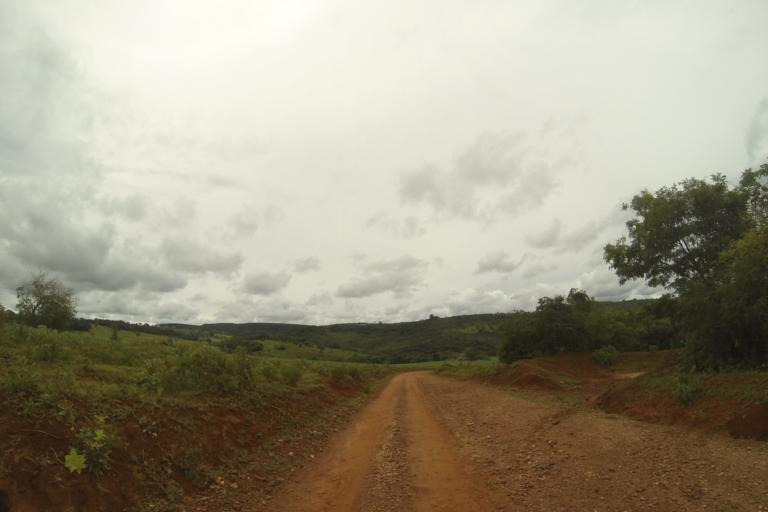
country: BR
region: Minas Gerais
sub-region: Ibia
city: Ibia
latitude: -19.6589
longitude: -46.7013
